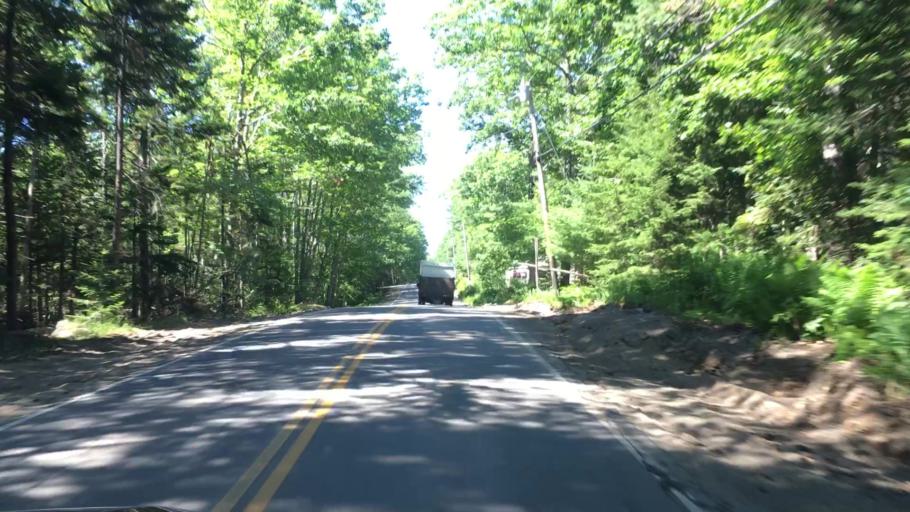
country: US
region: Maine
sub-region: Hancock County
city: Sedgwick
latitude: 44.3659
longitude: -68.5696
